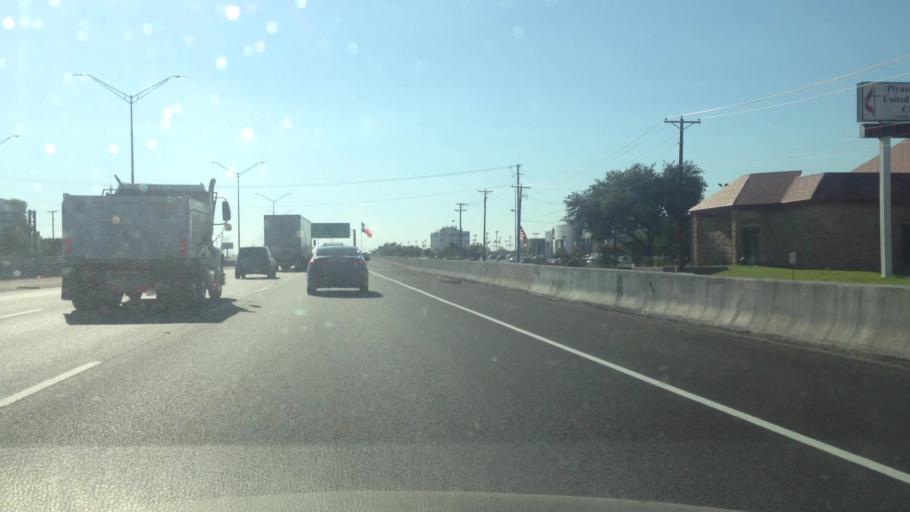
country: US
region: Texas
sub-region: Dallas County
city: Irving
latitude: 32.8375
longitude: -96.9669
